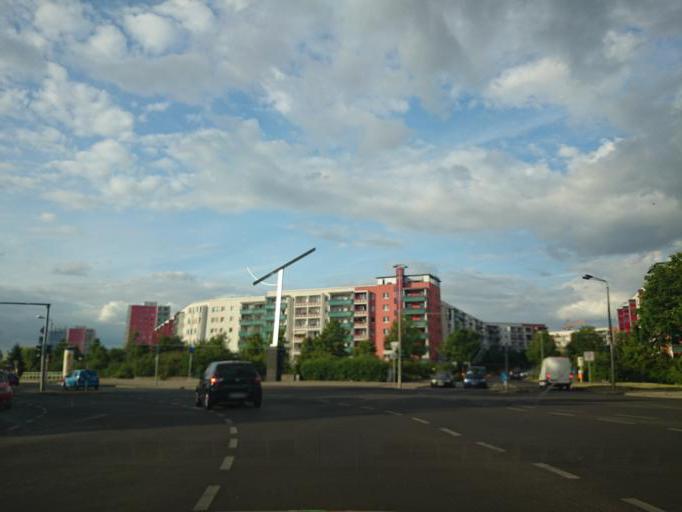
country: DE
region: Berlin
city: Kaulsdorf
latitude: 52.5174
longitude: 13.5890
